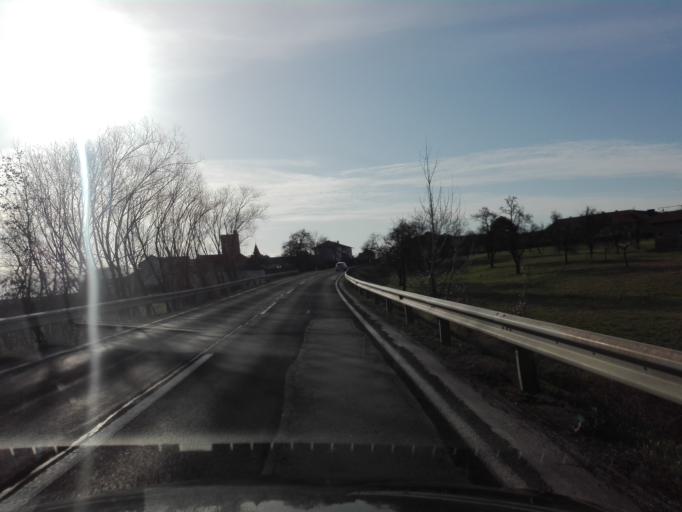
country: AT
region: Lower Austria
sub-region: Politischer Bezirk Amstetten
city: Strengberg
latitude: 48.1609
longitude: 14.6163
